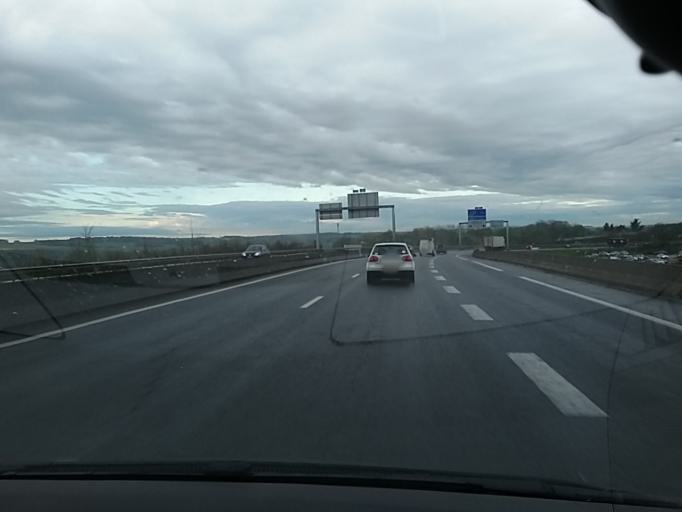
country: FR
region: Picardie
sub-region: Departement de la Somme
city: Boves
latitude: 49.8598
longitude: 2.3832
